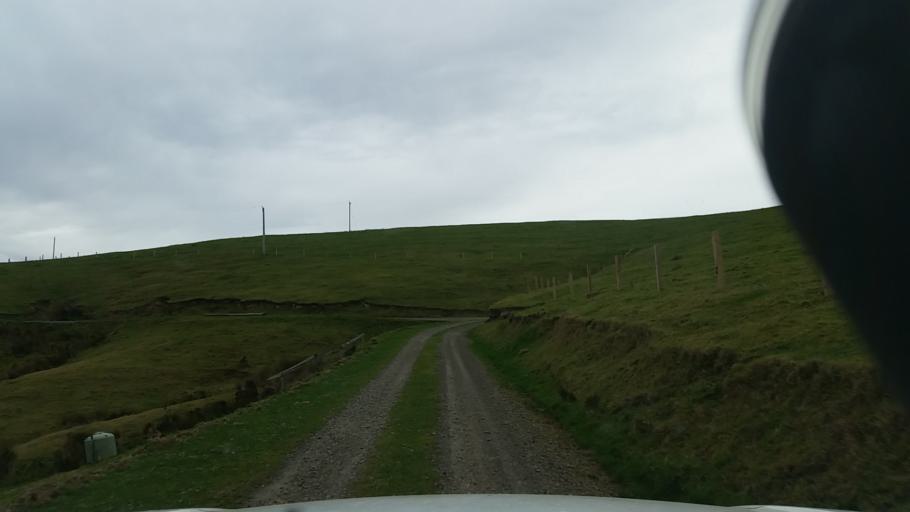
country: NZ
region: Canterbury
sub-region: Christchurch City
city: Christchurch
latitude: -43.8611
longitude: 173.0285
